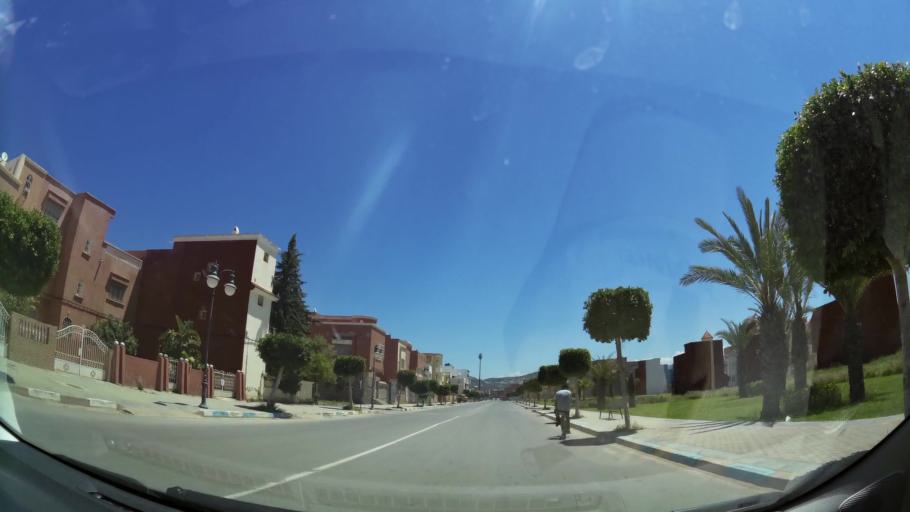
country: MA
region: Oriental
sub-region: Berkane-Taourirt
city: Madagh
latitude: 35.0802
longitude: -2.2329
